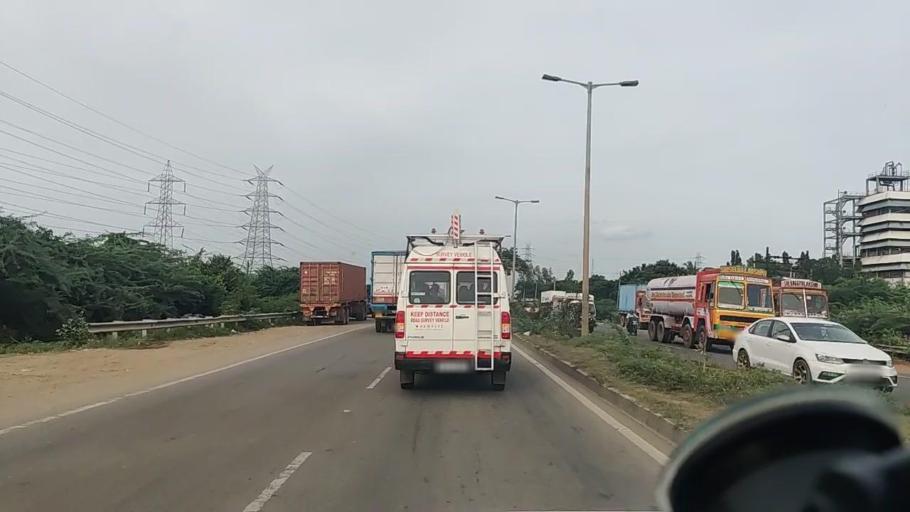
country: IN
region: Tamil Nadu
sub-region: Thiruvallur
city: Manali
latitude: 13.1800
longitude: 80.2563
